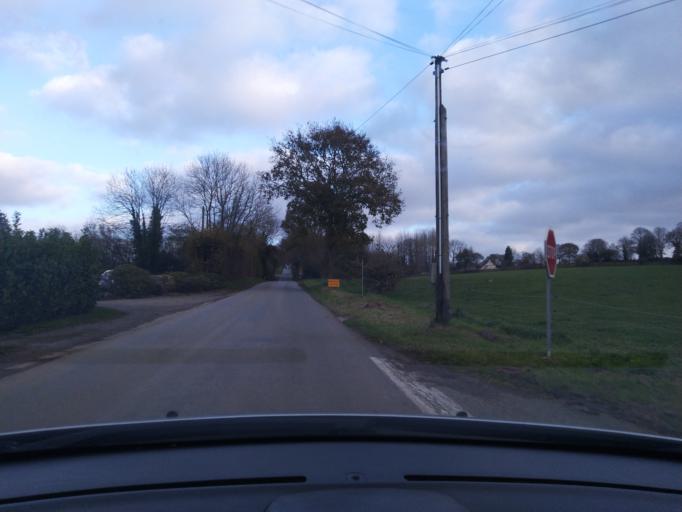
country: FR
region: Brittany
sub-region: Departement du Finistere
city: Plouigneau
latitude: 48.5664
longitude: -3.6597
